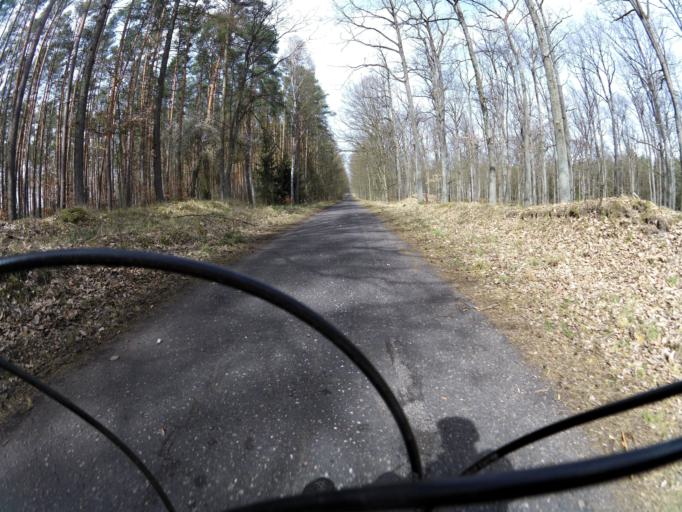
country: PL
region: West Pomeranian Voivodeship
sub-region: Powiat mysliborski
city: Boleszkowice
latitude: 52.7004
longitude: 14.5135
